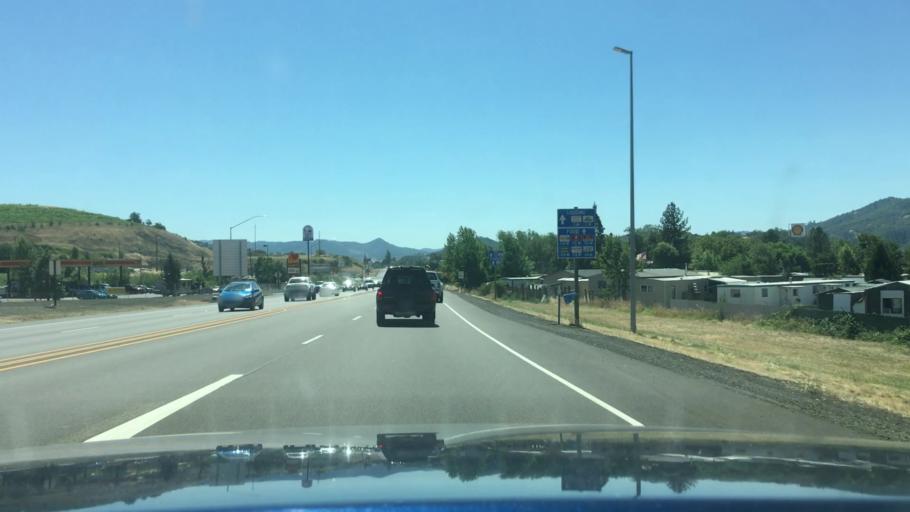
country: US
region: Oregon
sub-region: Douglas County
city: Green
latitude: 43.1511
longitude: -123.3669
